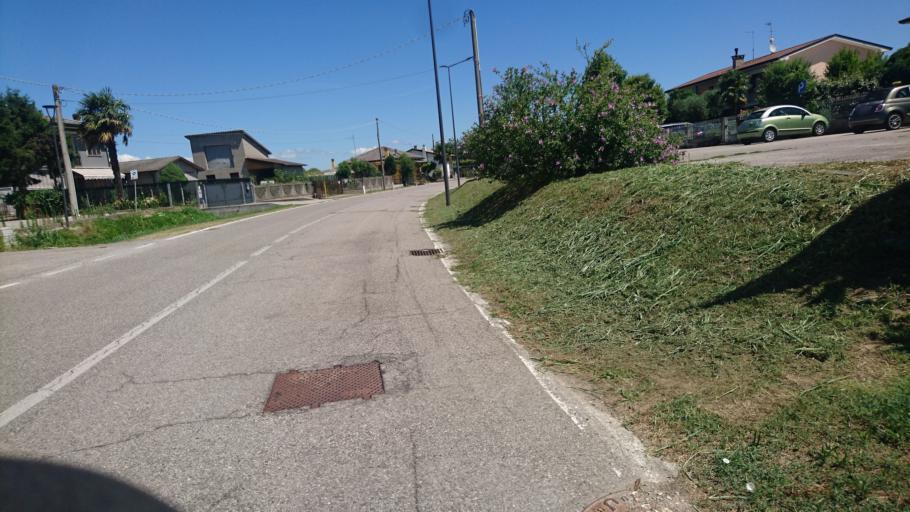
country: IT
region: Veneto
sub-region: Provincia di Padova
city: Campagnola
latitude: 45.2847
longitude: 12.0057
